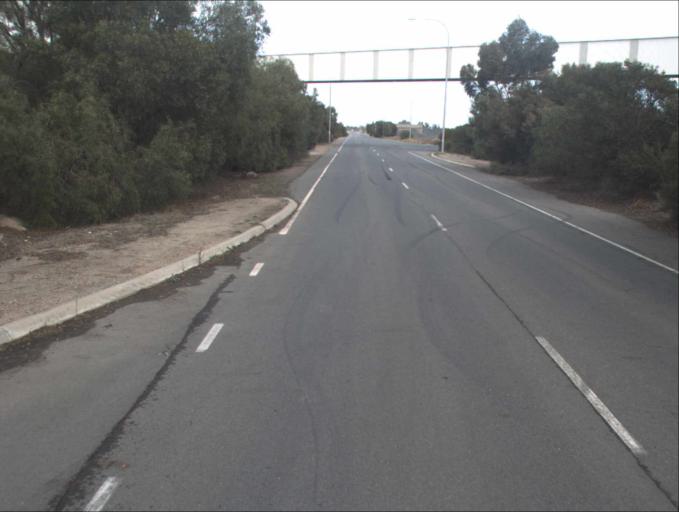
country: AU
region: South Australia
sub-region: Port Adelaide Enfield
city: Birkenhead
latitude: -34.7687
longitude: 138.5016
